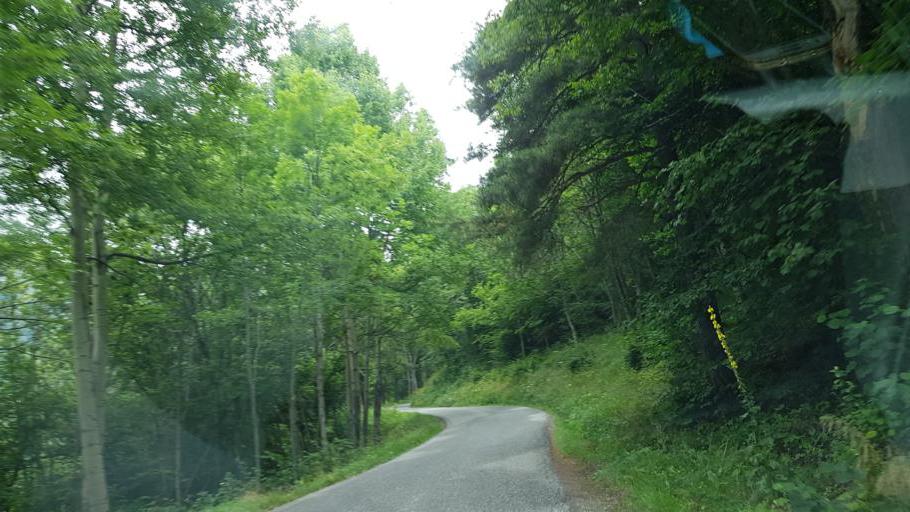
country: IT
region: Piedmont
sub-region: Provincia di Cuneo
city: Stroppo
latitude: 44.5115
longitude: 7.1287
